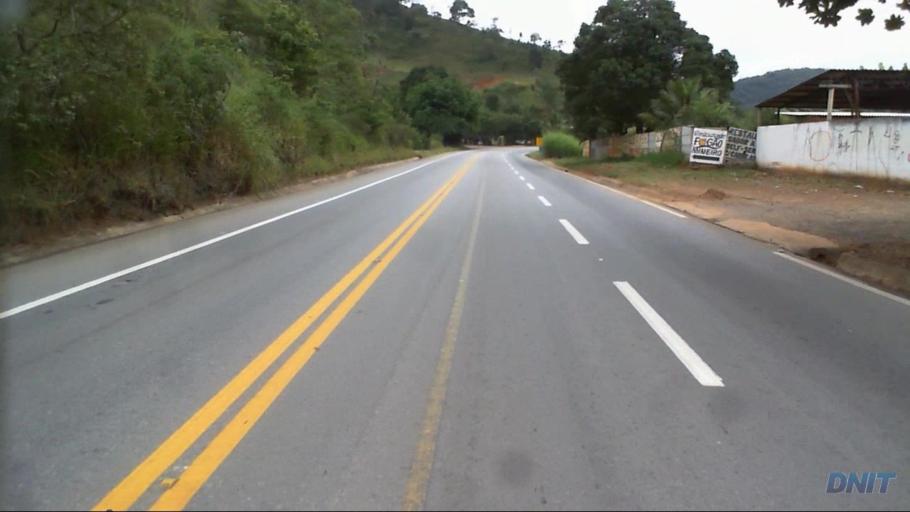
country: BR
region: Minas Gerais
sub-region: Timoteo
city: Timoteo
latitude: -19.6343
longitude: -42.8323
